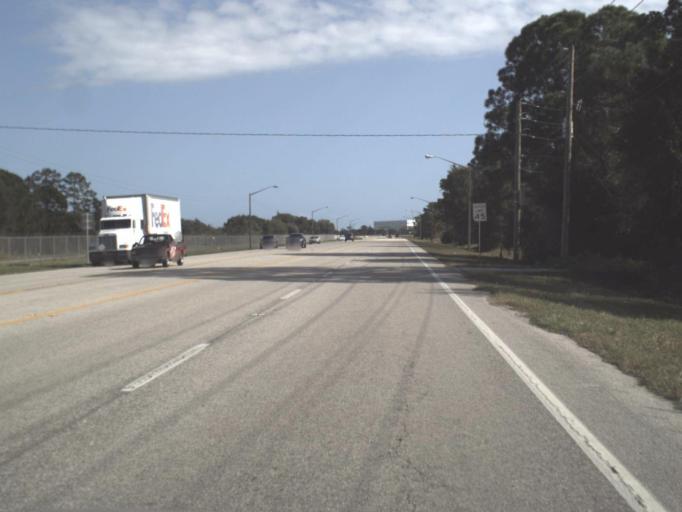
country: US
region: Florida
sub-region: Brevard County
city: West Melbourne
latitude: 28.0978
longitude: -80.6636
